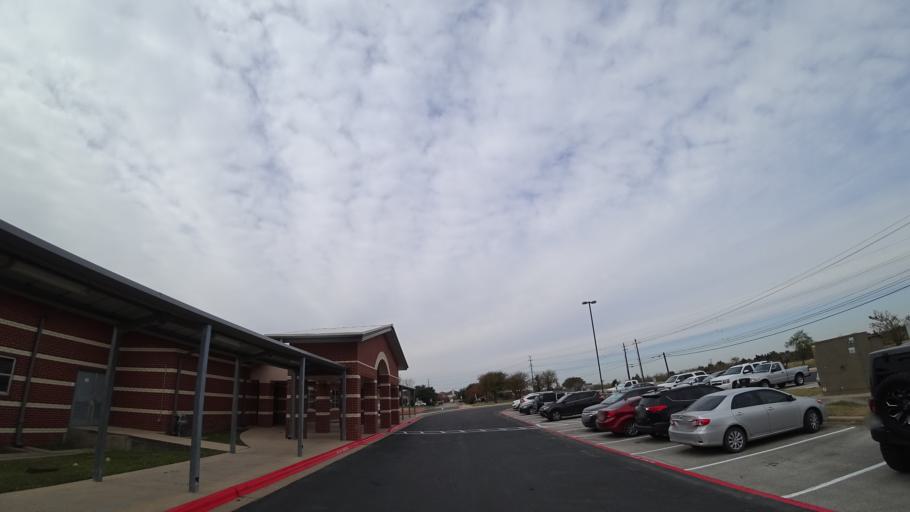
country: US
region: Texas
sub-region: Travis County
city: Garfield
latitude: 30.1580
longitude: -97.6436
